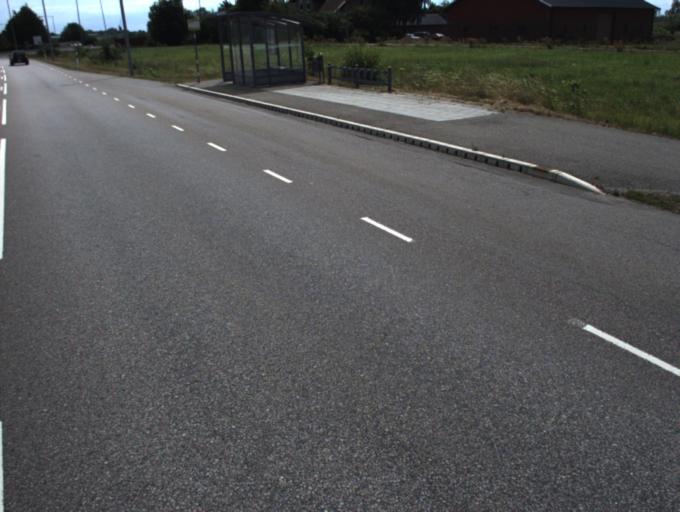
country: SE
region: Skane
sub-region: Helsingborg
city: Rydeback
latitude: 55.9658
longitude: 12.7857
